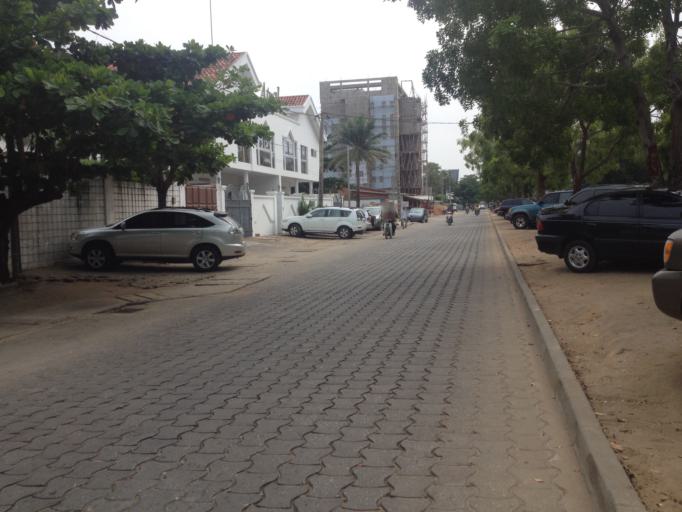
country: BJ
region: Littoral
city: Cotonou
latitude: 6.3566
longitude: 2.4060
